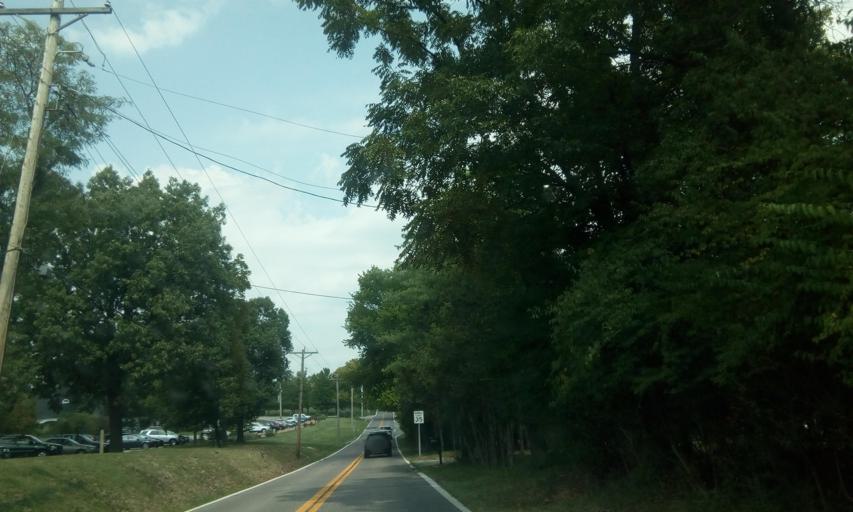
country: US
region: Missouri
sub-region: Saint Louis County
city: Town and Country
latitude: 38.6089
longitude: -90.4852
